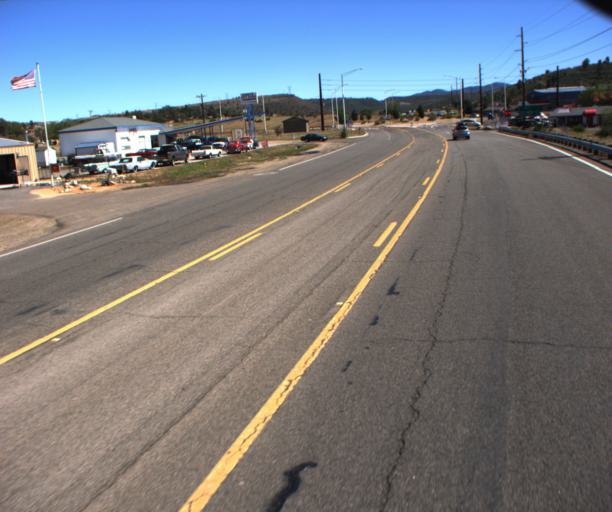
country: US
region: Arizona
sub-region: Yavapai County
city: Prescott
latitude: 34.5942
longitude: -112.4264
